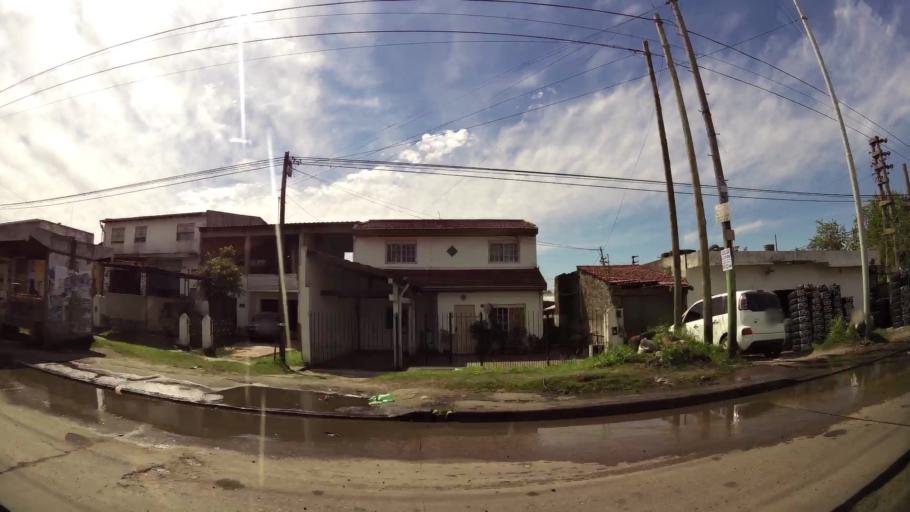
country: AR
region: Buenos Aires
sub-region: Partido de Almirante Brown
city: Adrogue
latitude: -34.7896
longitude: -58.3087
